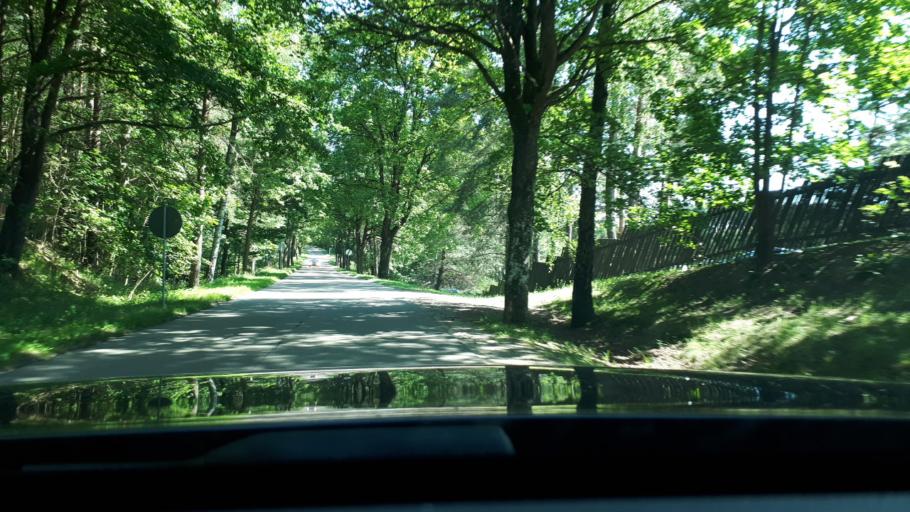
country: PL
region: Warmian-Masurian Voivodeship
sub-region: Powiat olsztynski
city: Stawiguda
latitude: 53.6133
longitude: 20.4166
